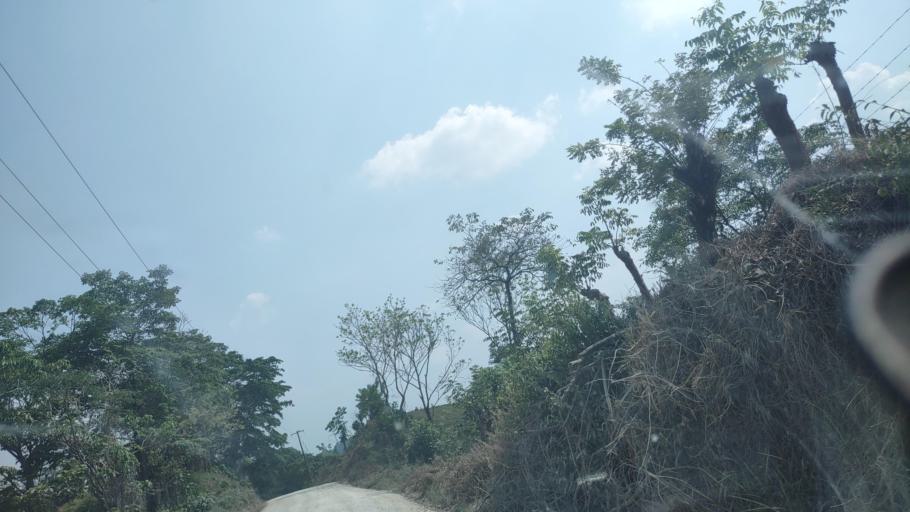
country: MX
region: Tabasco
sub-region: Huimanguillo
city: Francisco Rueda
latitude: 17.5848
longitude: -93.8921
